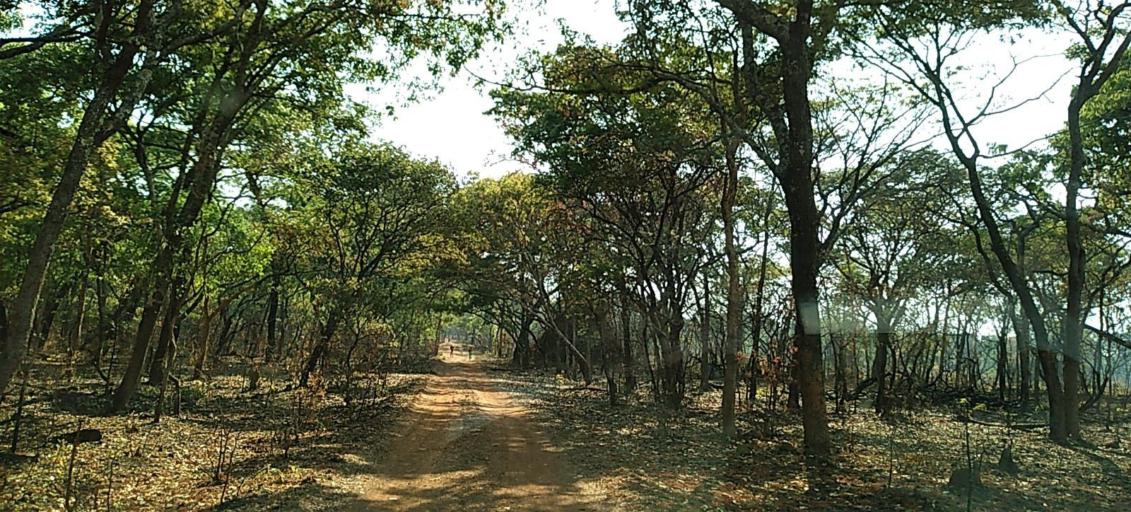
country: ZM
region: Copperbelt
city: Kalulushi
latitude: -13.0070
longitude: 27.7393
